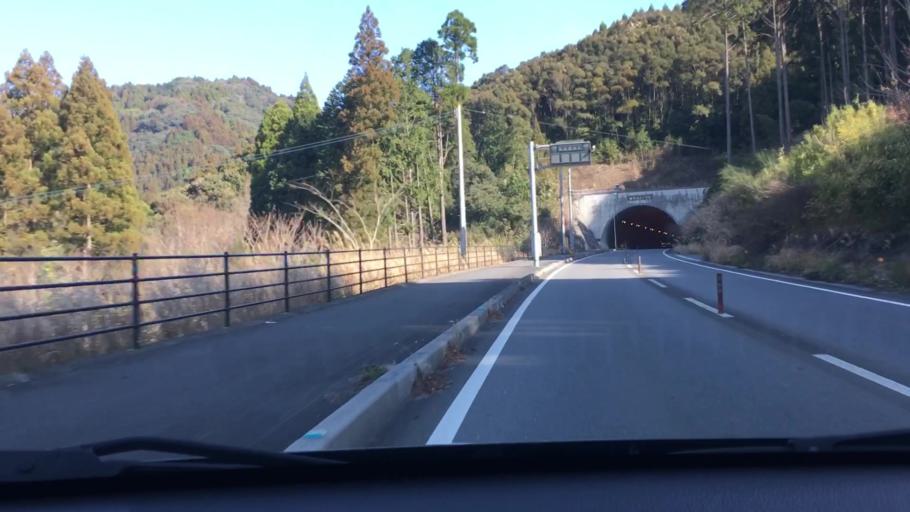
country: JP
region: Oita
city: Saiki
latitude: 32.9601
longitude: 131.8480
